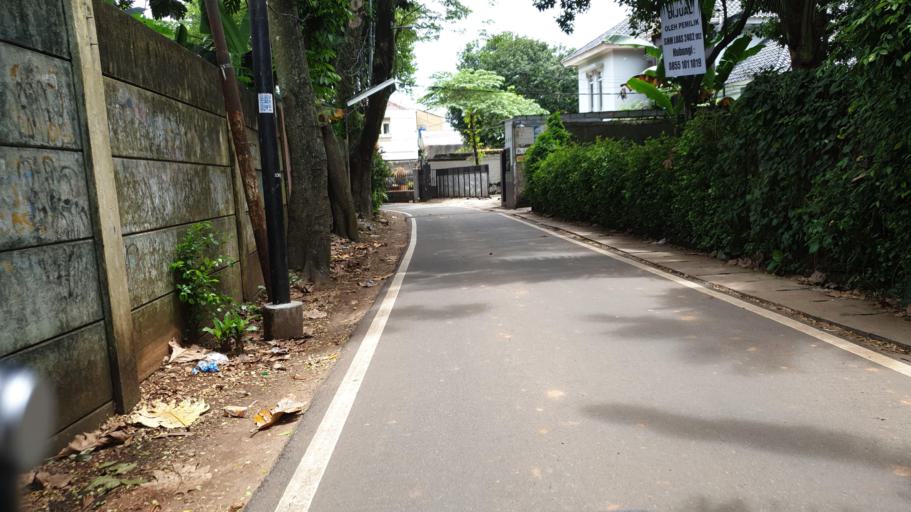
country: ID
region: West Java
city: Pamulang
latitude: -6.3092
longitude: 106.7816
